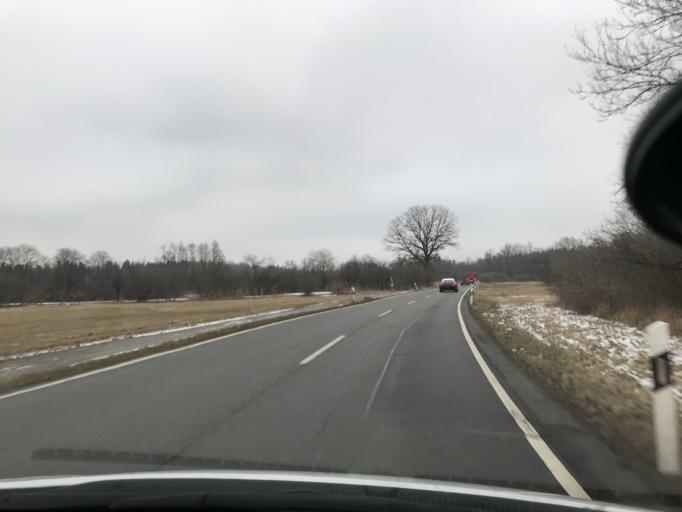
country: DE
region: Bavaria
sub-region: Upper Bavaria
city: Bad Feilnbach
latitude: 47.7985
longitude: 12.0158
